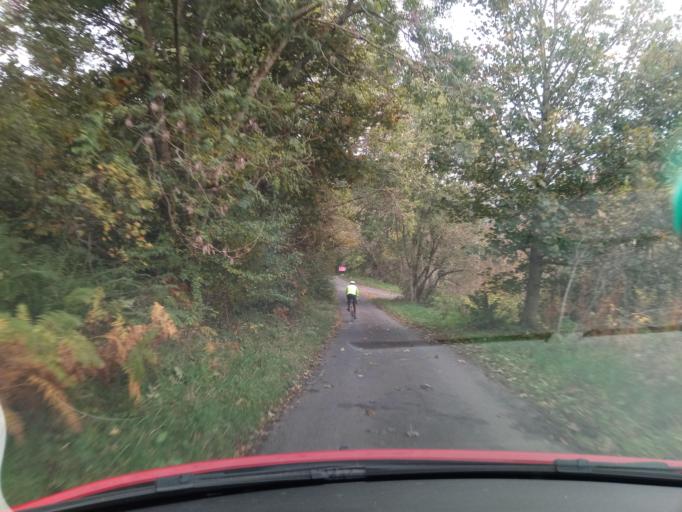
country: GB
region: Scotland
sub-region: The Scottish Borders
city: Innerleithen
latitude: 55.6191
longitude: -3.0161
